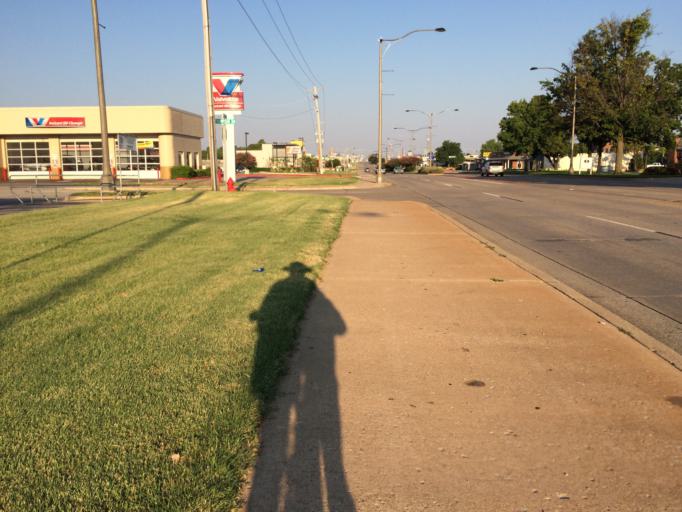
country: US
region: Oklahoma
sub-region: Cleveland County
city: Norman
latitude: 35.2184
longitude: -97.4700
